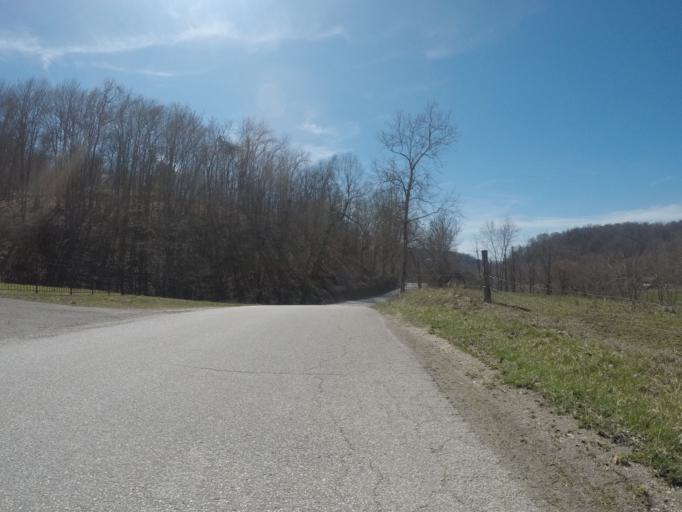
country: US
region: Ohio
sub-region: Lawrence County
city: South Point
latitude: 38.4711
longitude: -82.5665
